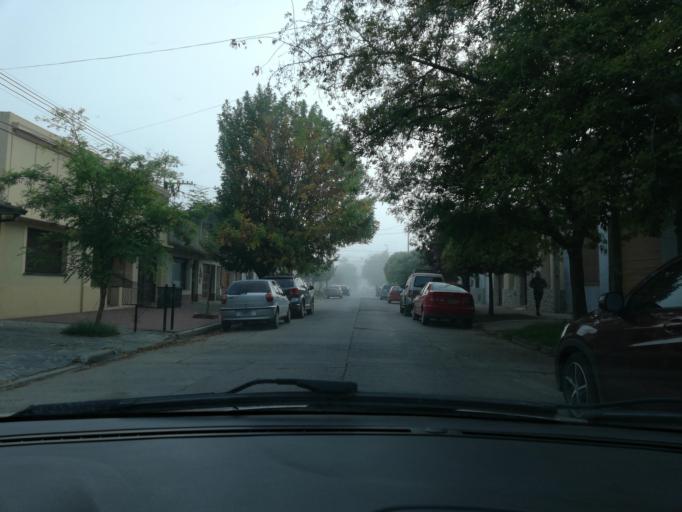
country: AR
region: Buenos Aires
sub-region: Partido de Balcarce
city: Balcarce
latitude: -37.8447
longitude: -58.2512
